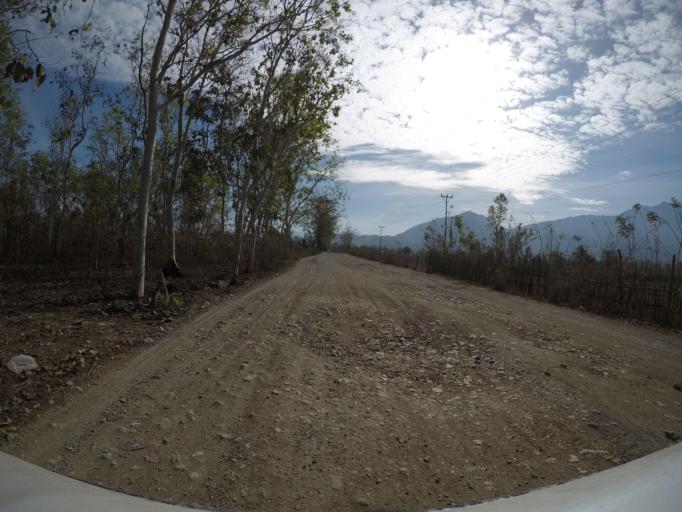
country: TL
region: Bobonaro
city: Maliana
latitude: -8.9306
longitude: 125.2004
